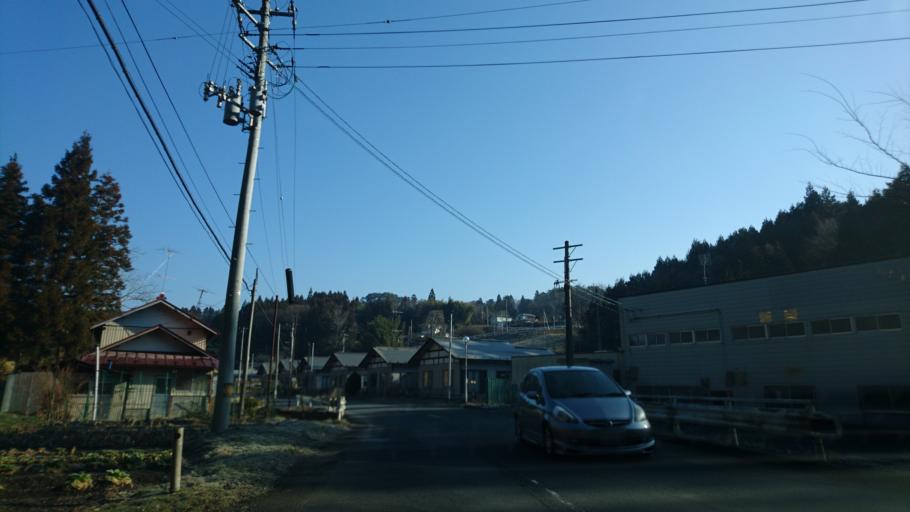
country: JP
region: Iwate
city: Ichinoseki
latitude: 38.9042
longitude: 141.2798
